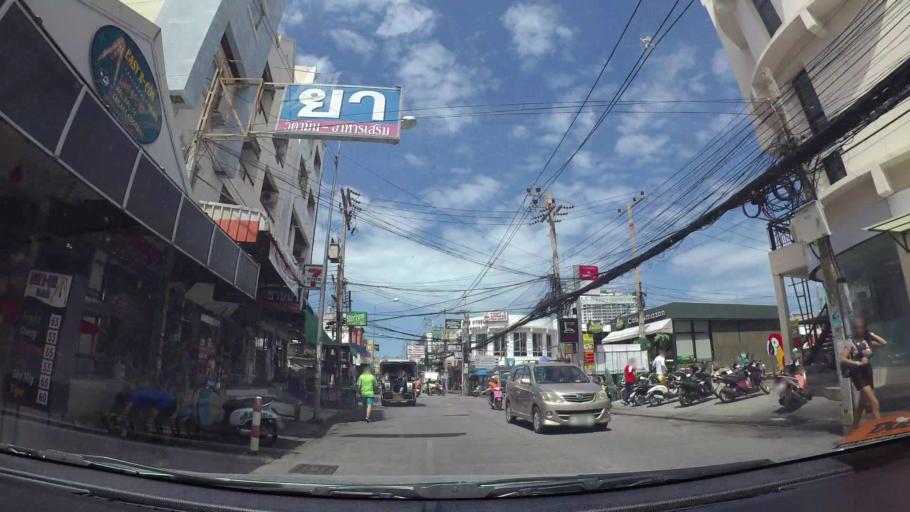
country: TH
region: Chon Buri
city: Phatthaya
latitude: 12.9328
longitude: 100.8872
